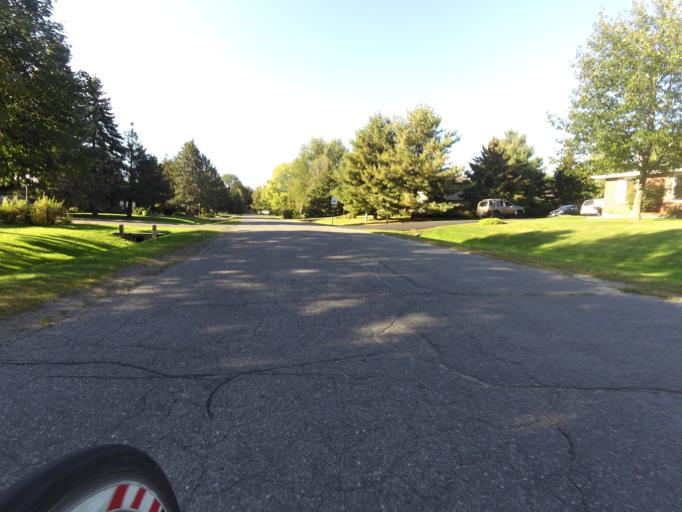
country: CA
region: Ontario
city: Bells Corners
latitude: 45.2223
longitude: -75.6929
